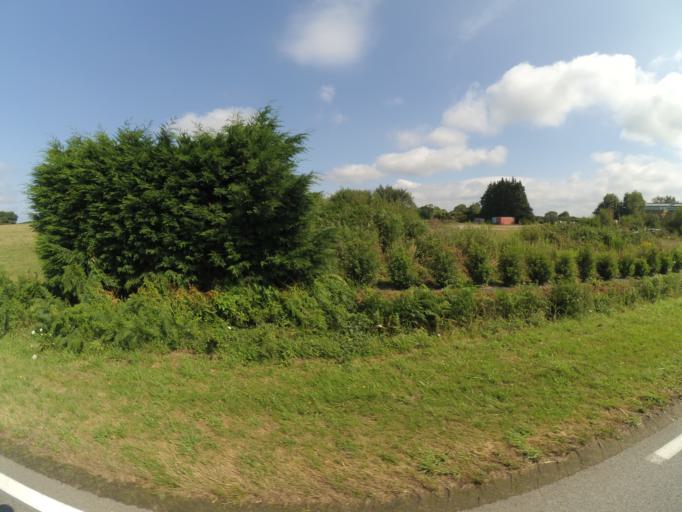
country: FR
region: Brittany
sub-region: Departement du Finistere
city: Le Trevoux
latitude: 47.9209
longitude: -3.6596
